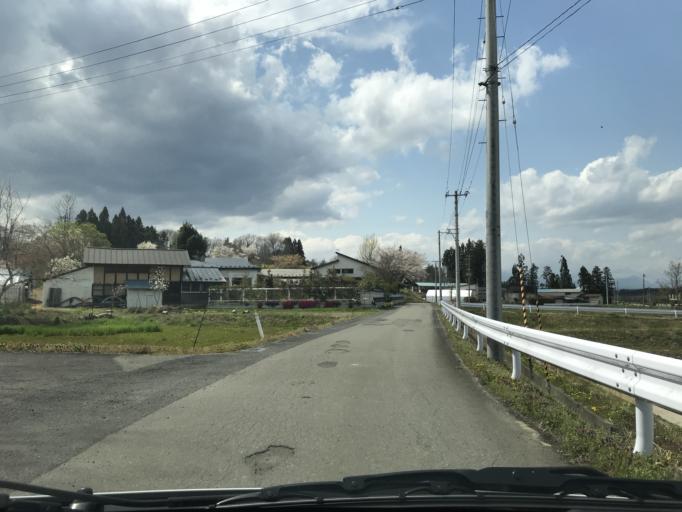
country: JP
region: Iwate
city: Mizusawa
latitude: 39.0666
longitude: 141.1063
